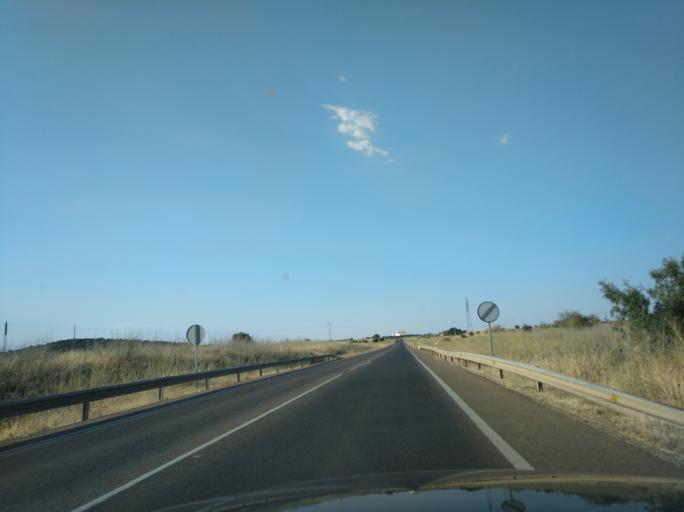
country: ES
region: Extremadura
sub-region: Provincia de Badajoz
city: Olivenza
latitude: 38.6987
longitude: -7.0894
